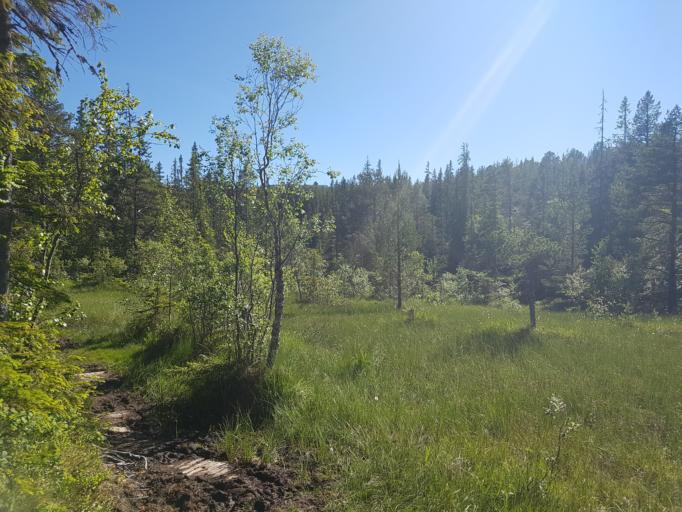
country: NO
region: Sor-Trondelag
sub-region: Trondheim
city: Trondheim
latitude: 63.4375
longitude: 10.2714
